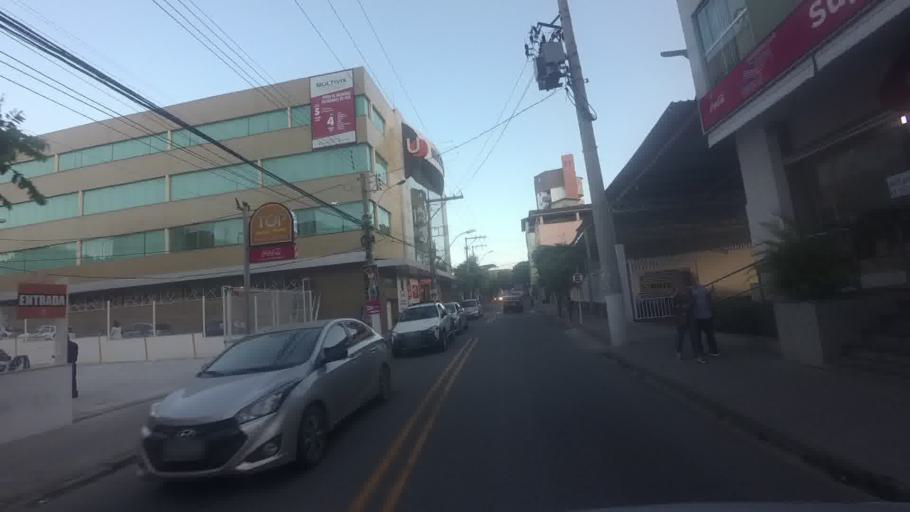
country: BR
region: Espirito Santo
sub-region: Cachoeiro De Itapemirim
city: Cachoeiro de Itapemirim
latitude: -20.8500
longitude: -41.1093
